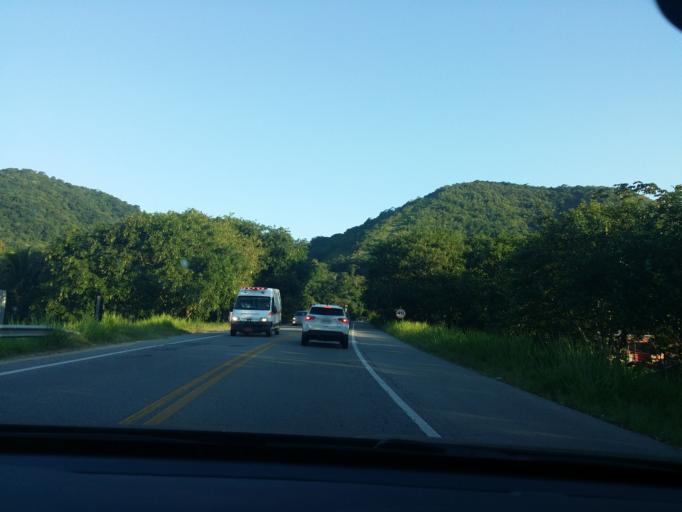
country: BR
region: Sao Paulo
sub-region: Sao Sebastiao
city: Sao Sebastiao
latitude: -23.7694
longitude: -45.6400
